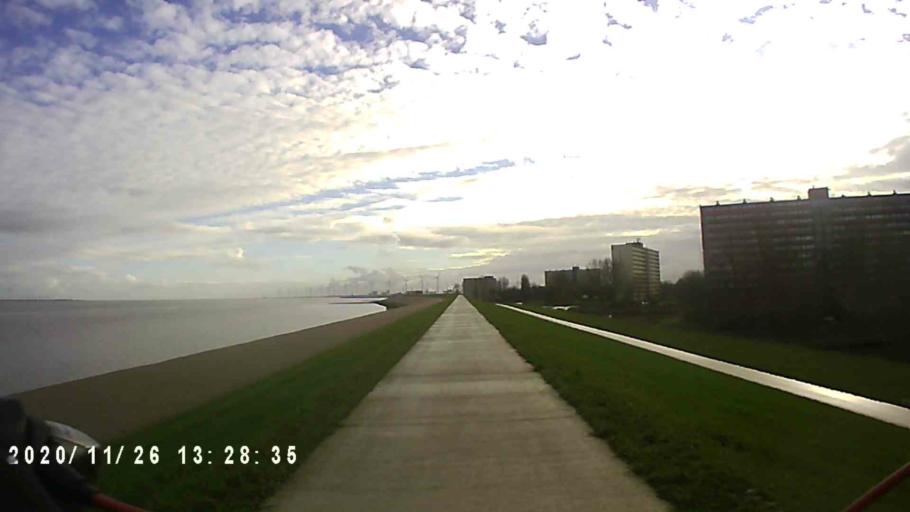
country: NL
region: Groningen
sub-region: Gemeente Delfzijl
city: Delfzijl
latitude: 53.3460
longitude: 6.9097
